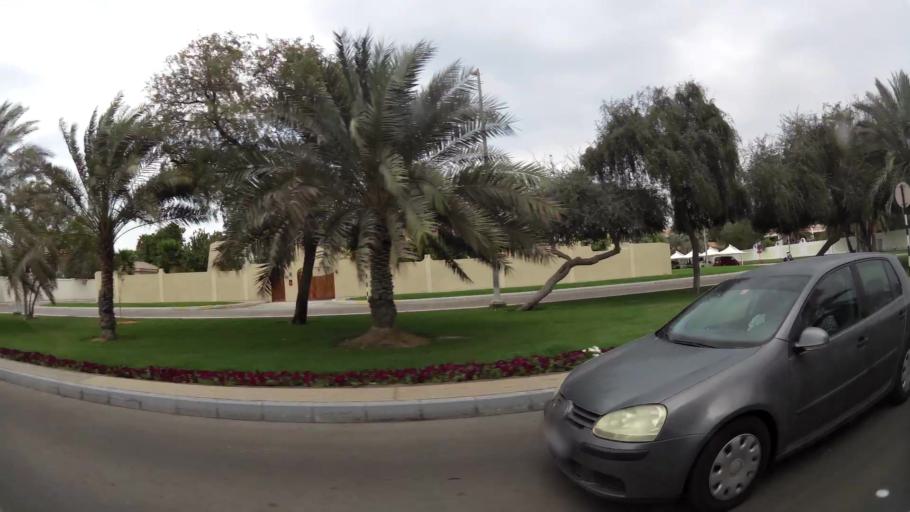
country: AE
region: Abu Dhabi
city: Abu Dhabi
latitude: 24.4367
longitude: 54.3652
